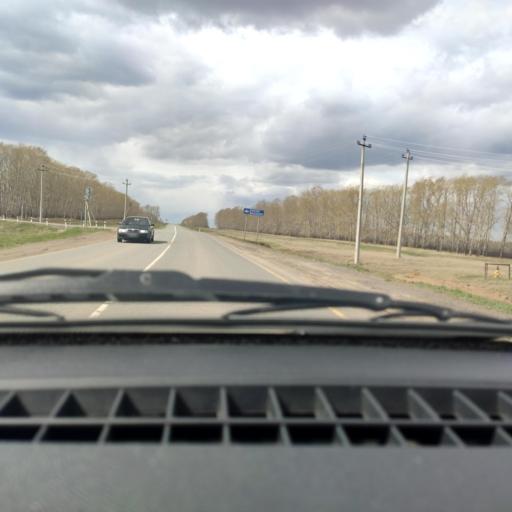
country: RU
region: Bashkortostan
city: Alekseyevka
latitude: 55.0546
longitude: 55.1213
